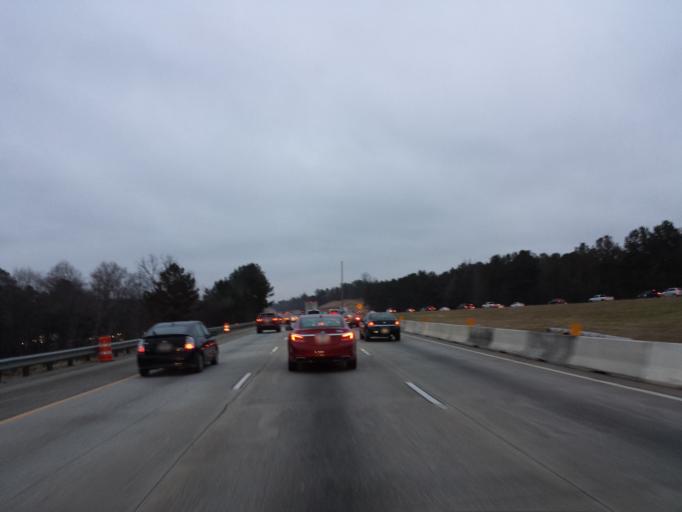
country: US
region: Georgia
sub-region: Henry County
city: Stockbridge
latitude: 33.5402
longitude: -84.2671
